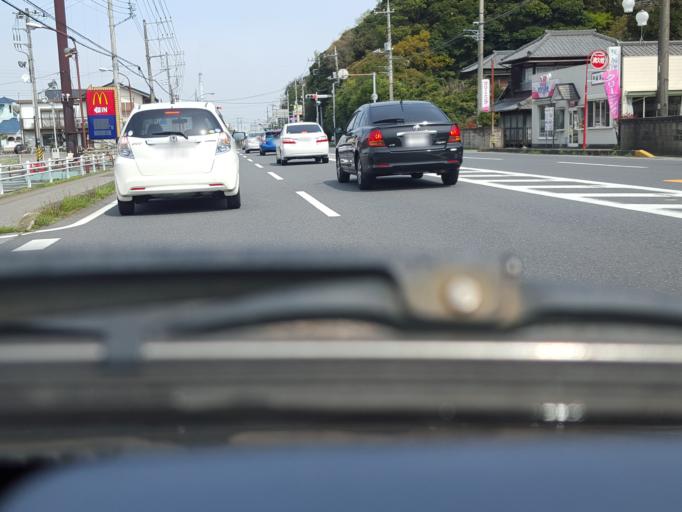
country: JP
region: Chiba
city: Ichihara
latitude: 35.4651
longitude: 140.0455
